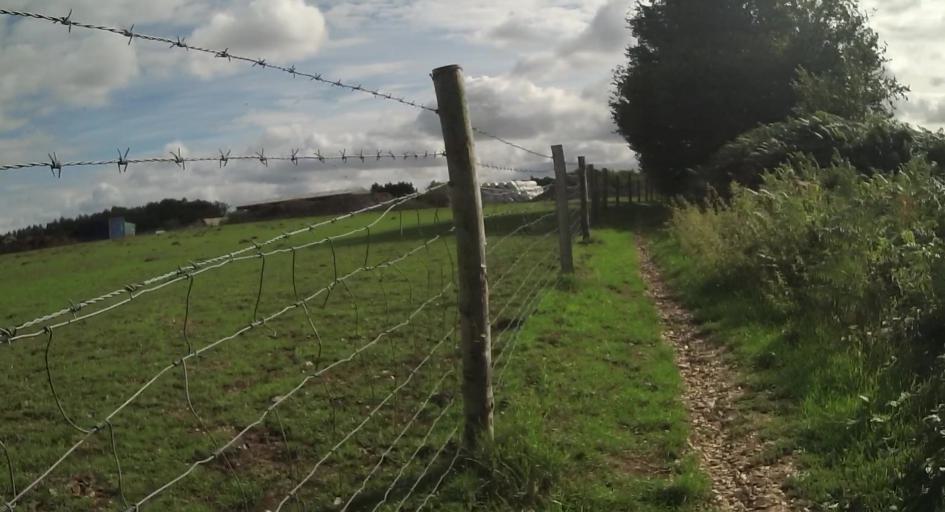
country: GB
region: England
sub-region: West Berkshire
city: Thatcham
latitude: 51.3819
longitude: -1.2397
